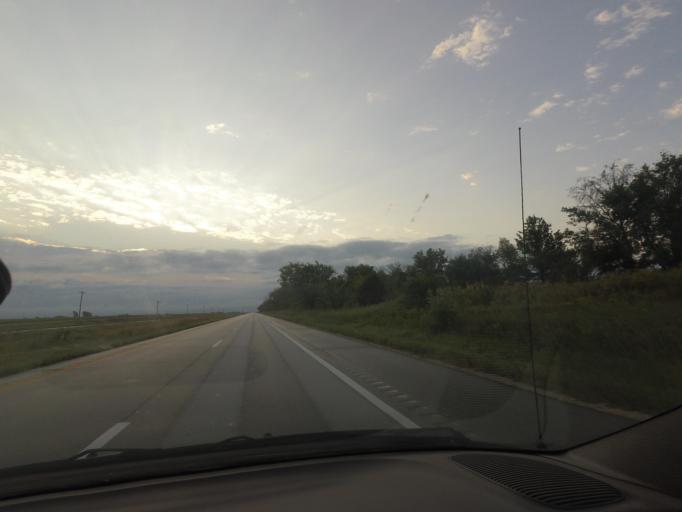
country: US
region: Missouri
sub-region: Shelby County
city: Shelbina
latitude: 39.7166
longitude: -92.1383
